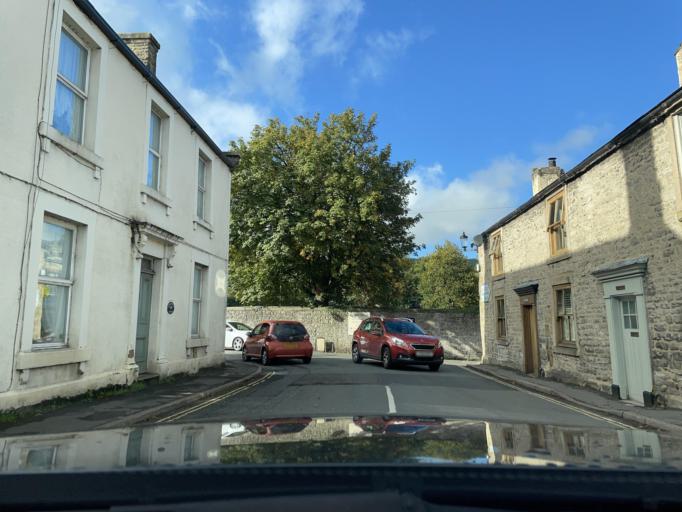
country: GB
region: England
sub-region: Derbyshire
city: Hope Valley
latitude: 53.3439
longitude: -1.7749
